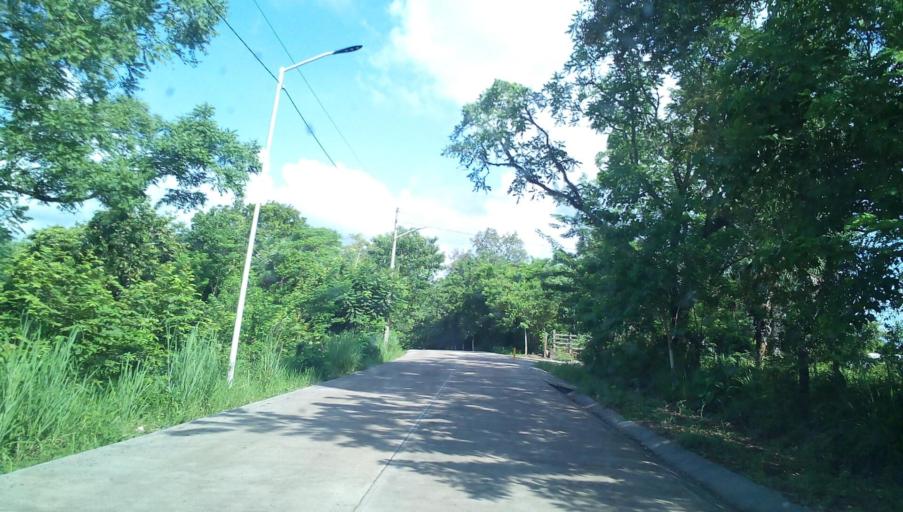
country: MX
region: Veracruz
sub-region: Citlaltepetl
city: Las Sabinas
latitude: 21.3387
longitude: -97.8837
